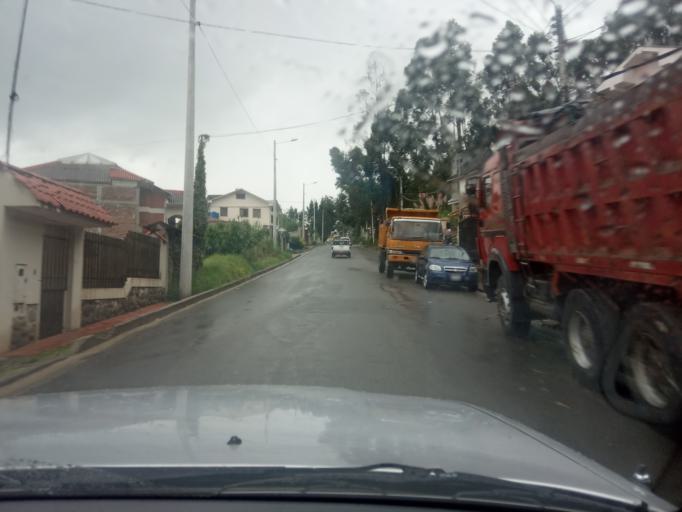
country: EC
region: Azuay
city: Llacao
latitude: -2.8619
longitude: -78.9378
